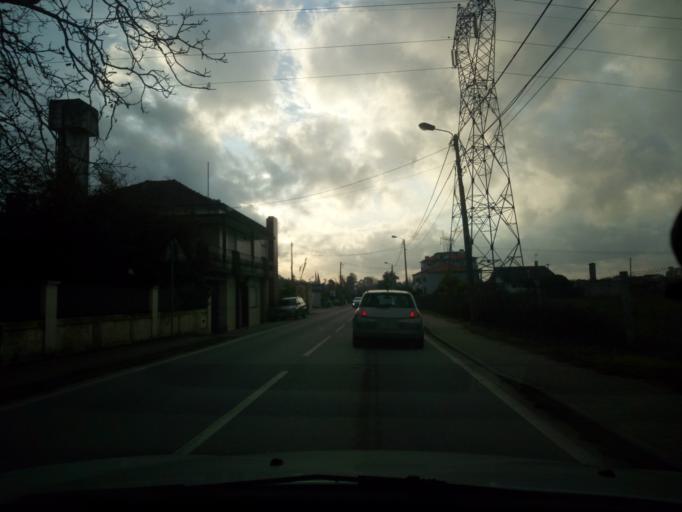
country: PT
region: Aveiro
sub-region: Agueda
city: Agueda
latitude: 40.5588
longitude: -8.4689
